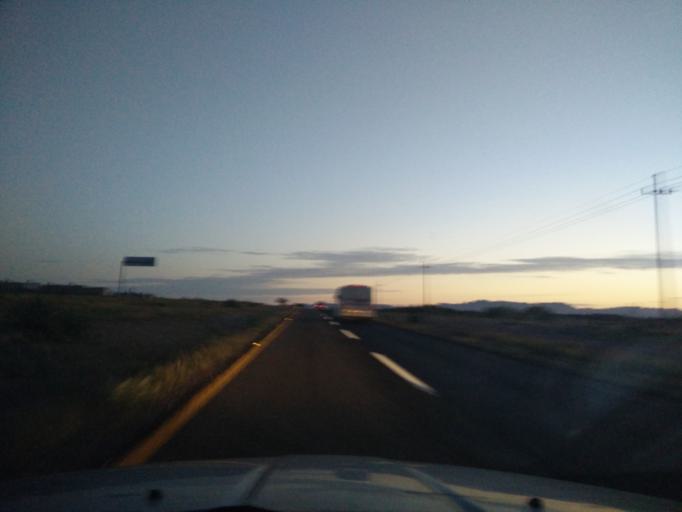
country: MX
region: Sonora
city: Heroica Guaymas
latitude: 28.0012
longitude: -110.9370
